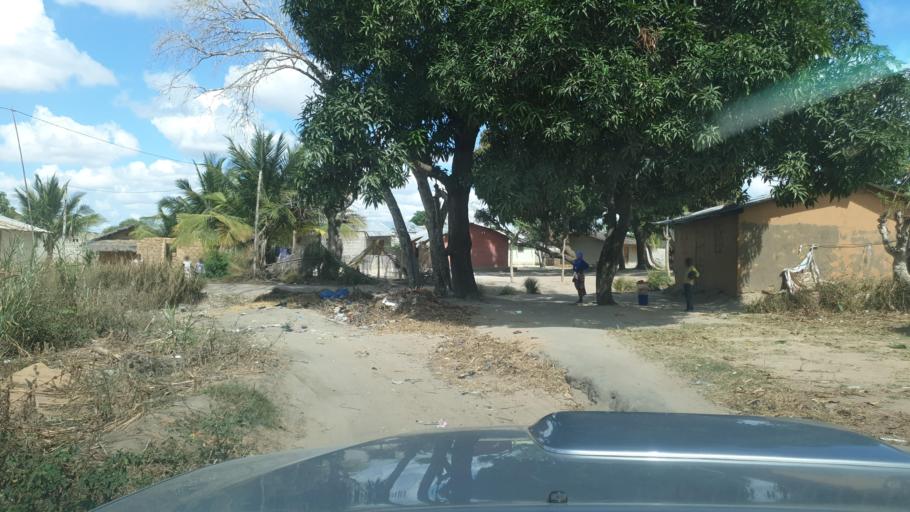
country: MZ
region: Nampula
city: Nacala
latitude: -14.5729
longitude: 40.6963
